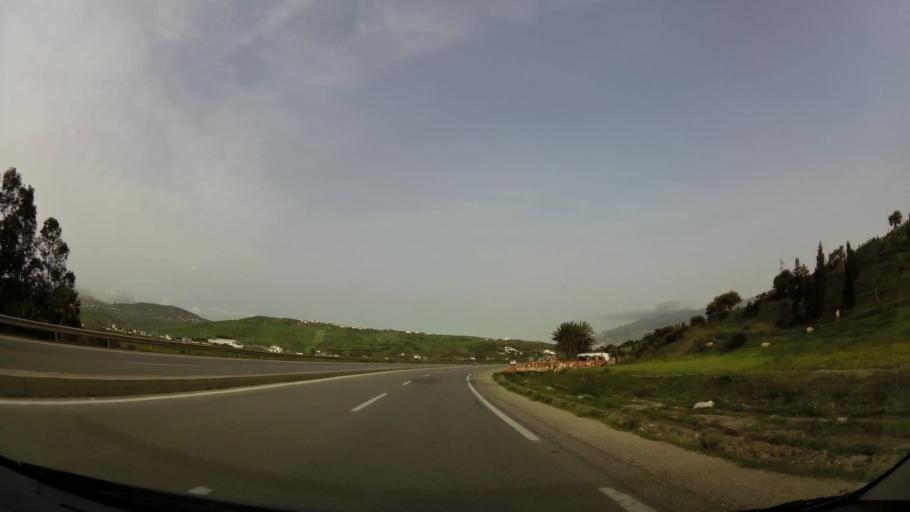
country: MA
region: Tanger-Tetouan
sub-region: Tetouan
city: Saddina
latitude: 35.5610
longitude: -5.4734
